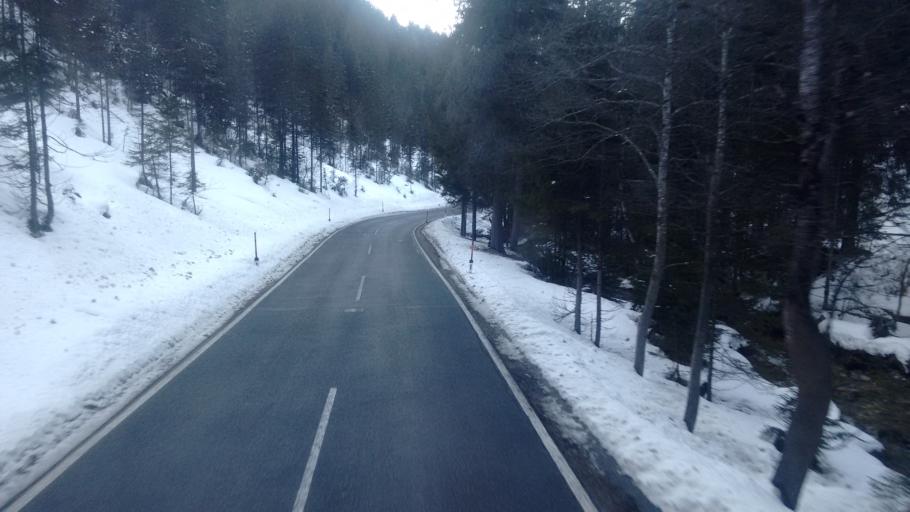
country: AT
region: Salzburg
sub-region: Politischer Bezirk Sankt Johann im Pongau
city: Radstadt
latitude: 47.3401
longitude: 13.4379
